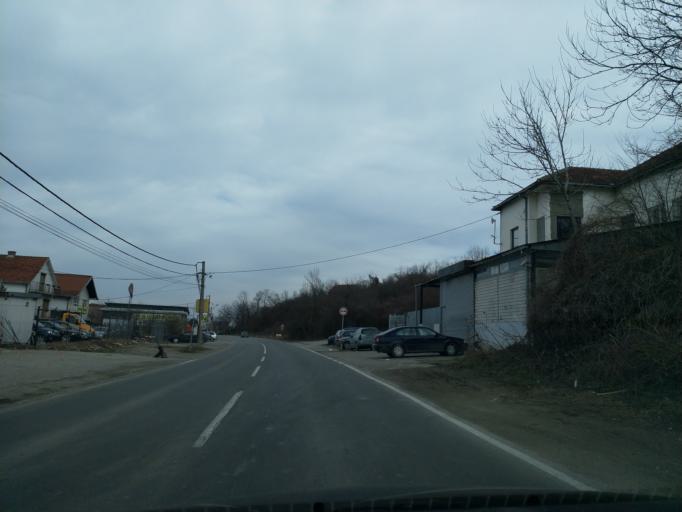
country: RS
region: Central Serbia
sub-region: Belgrade
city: Zvezdara
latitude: 44.7288
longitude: 20.5816
